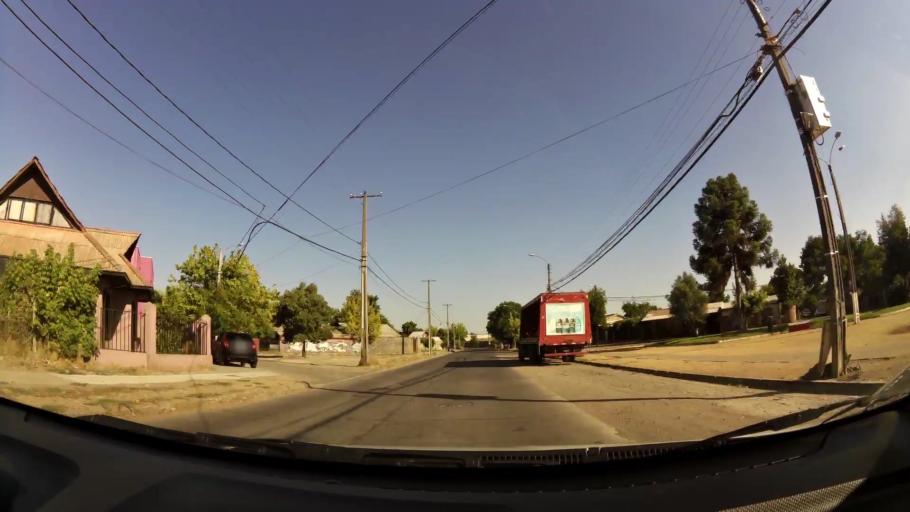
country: CL
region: Maule
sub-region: Provincia de Talca
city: Talca
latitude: -35.4411
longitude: -71.6697
